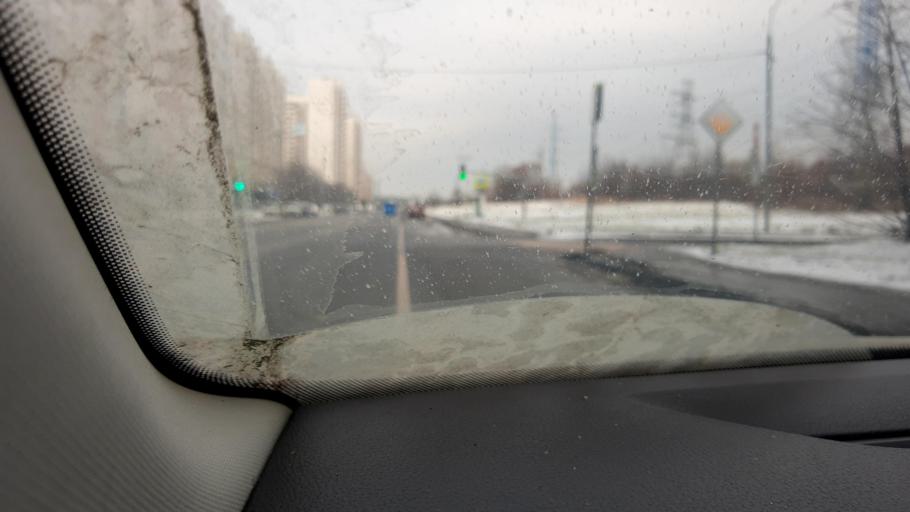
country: RU
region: Moscow
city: Annino
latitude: 55.5714
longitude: 37.5898
